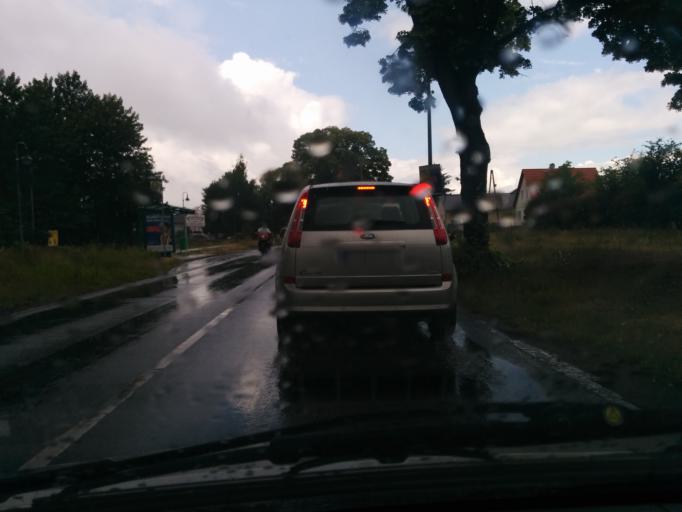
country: DE
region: Berlin
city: Staaken
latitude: 52.5594
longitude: 13.1307
